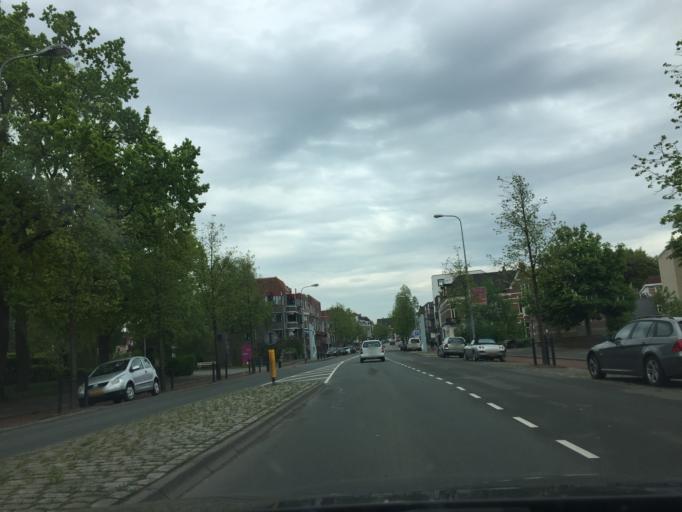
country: NL
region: Groningen
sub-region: Gemeente Groningen
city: Groningen
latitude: 53.2015
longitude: 6.5771
